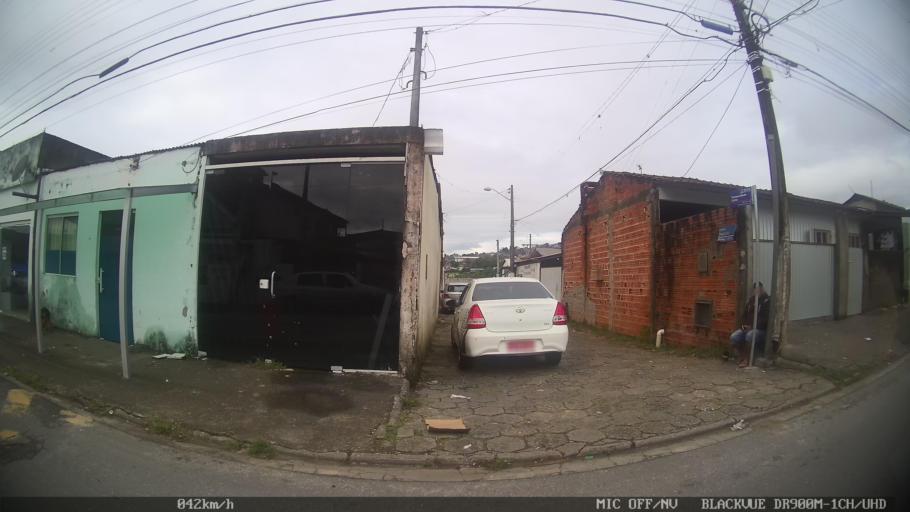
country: BR
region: Santa Catarina
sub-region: Biguacu
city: Biguacu
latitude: -27.5400
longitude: -48.6432
